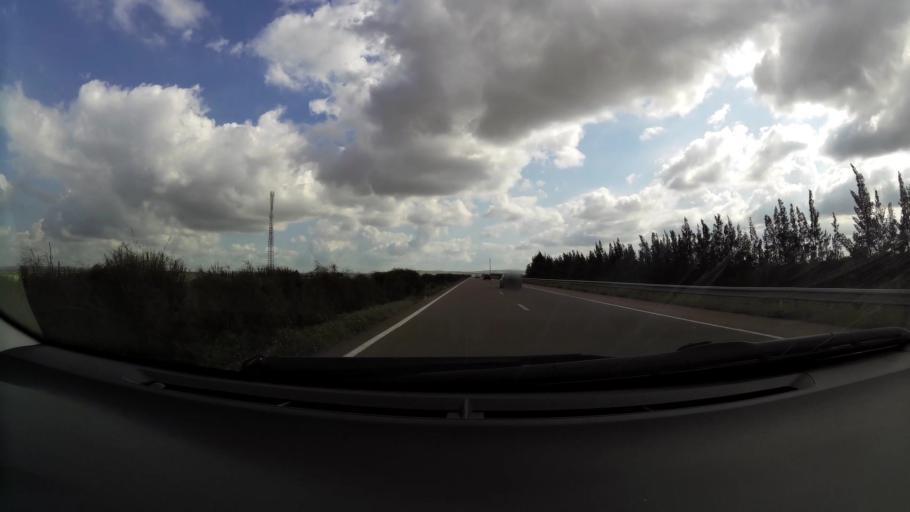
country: MA
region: Chaouia-Ouardigha
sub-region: Settat Province
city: Berrechid
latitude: 33.1450
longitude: -7.5742
